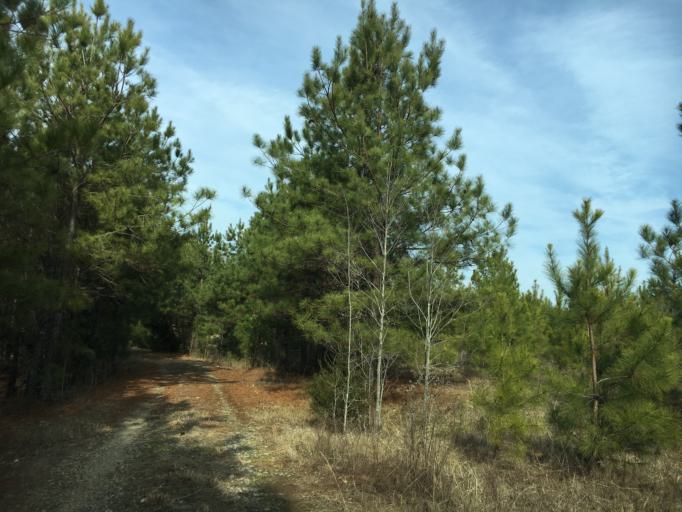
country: US
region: South Carolina
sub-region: Laurens County
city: Laurens
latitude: 34.3489
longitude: -82.0032
